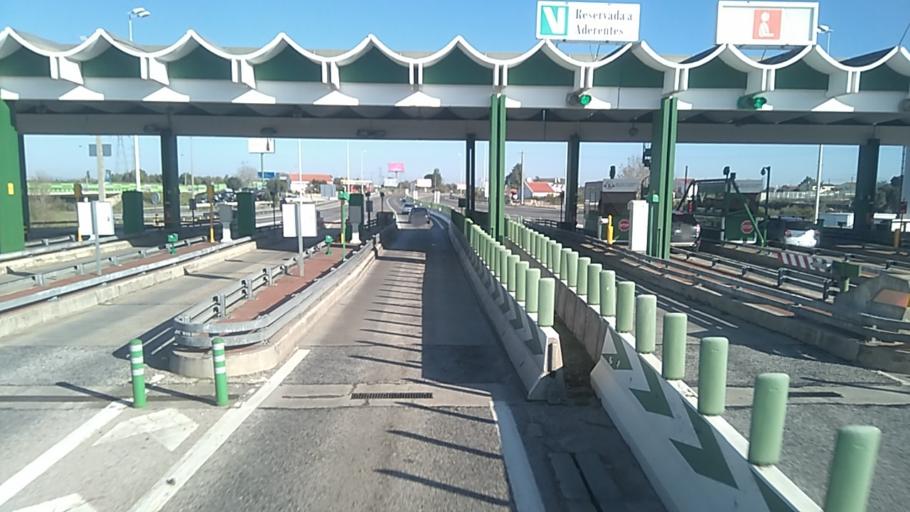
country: PT
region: Santarem
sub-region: Santarem
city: Santarem
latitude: 39.2604
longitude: -8.7310
